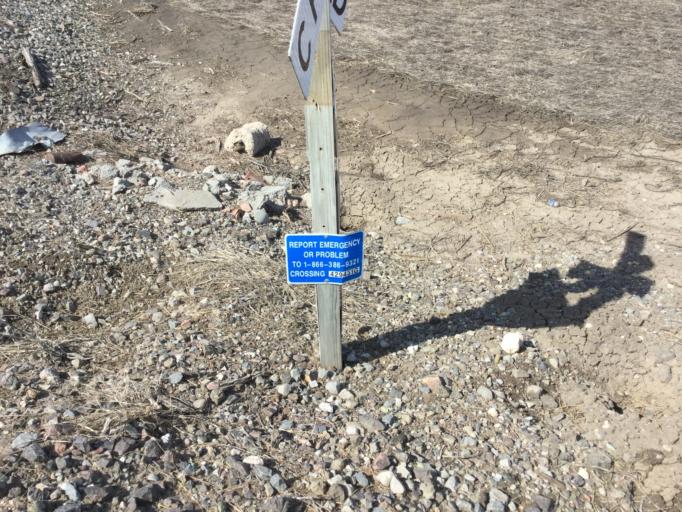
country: US
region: Kansas
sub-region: Scott County
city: Scott City
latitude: 38.5112
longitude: -100.8333
